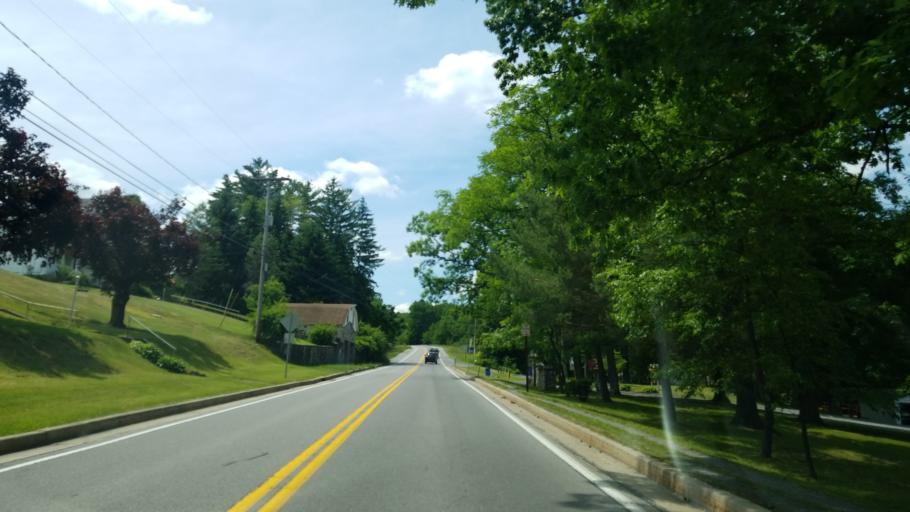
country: US
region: Pennsylvania
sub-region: Blair County
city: Tyrone
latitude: 40.6795
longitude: -78.2552
